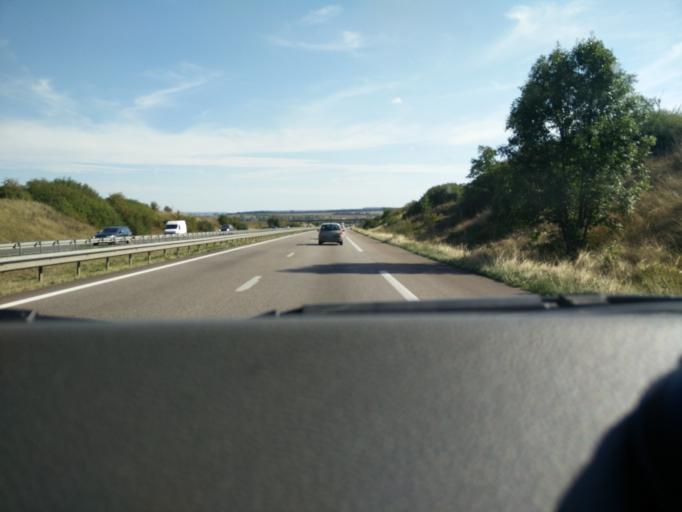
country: FR
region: Lorraine
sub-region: Departement de Meurthe-et-Moselle
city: Pont-a-Mousson
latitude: 48.9563
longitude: 6.1096
